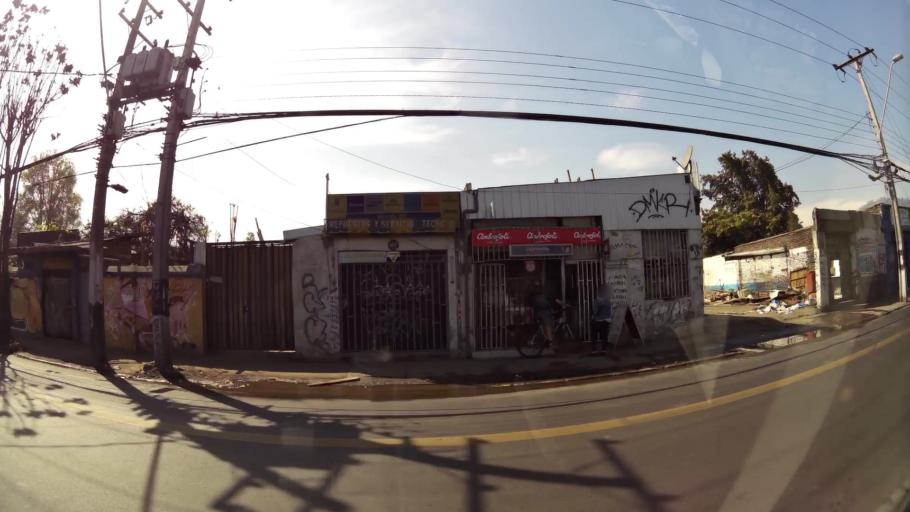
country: CL
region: Santiago Metropolitan
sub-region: Provincia de Santiago
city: Santiago
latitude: -33.3964
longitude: -70.6427
